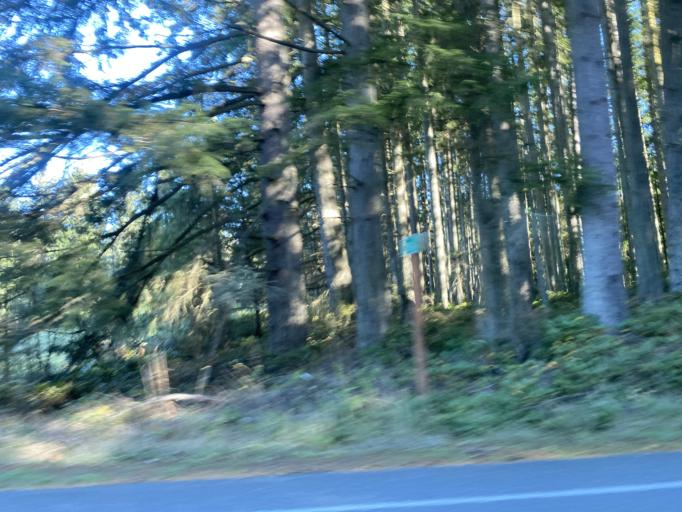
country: US
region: Washington
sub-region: Island County
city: Langley
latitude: 48.0075
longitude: -122.4260
